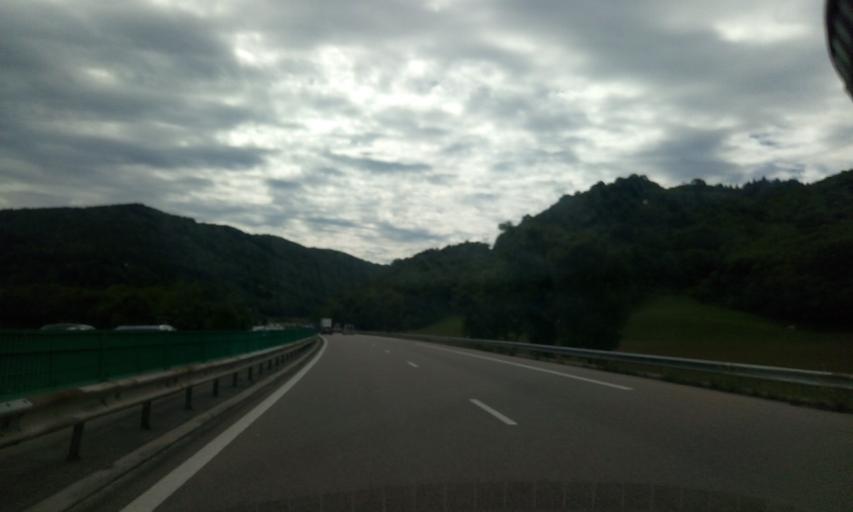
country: FR
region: Rhone-Alpes
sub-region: Departement de l'Isere
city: Colombe
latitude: 45.4200
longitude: 5.4514
